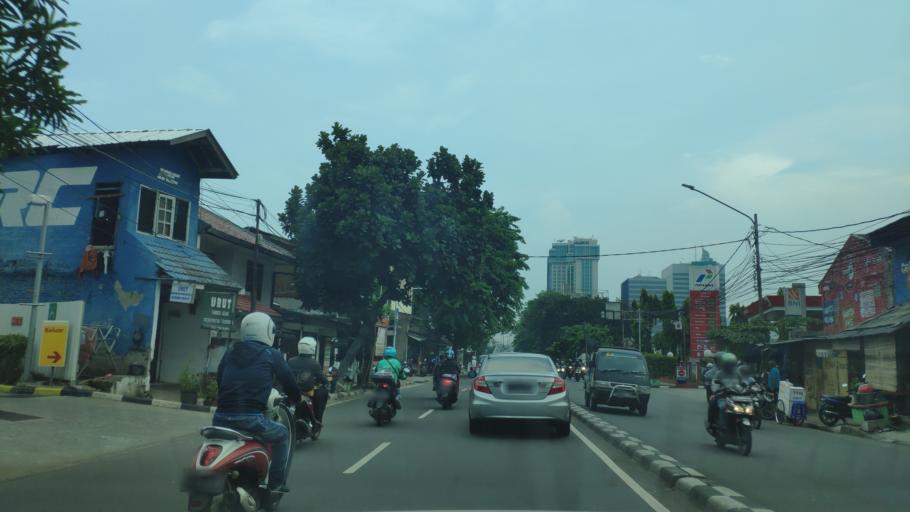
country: ID
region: Jakarta Raya
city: Jakarta
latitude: -6.1899
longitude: 106.7926
